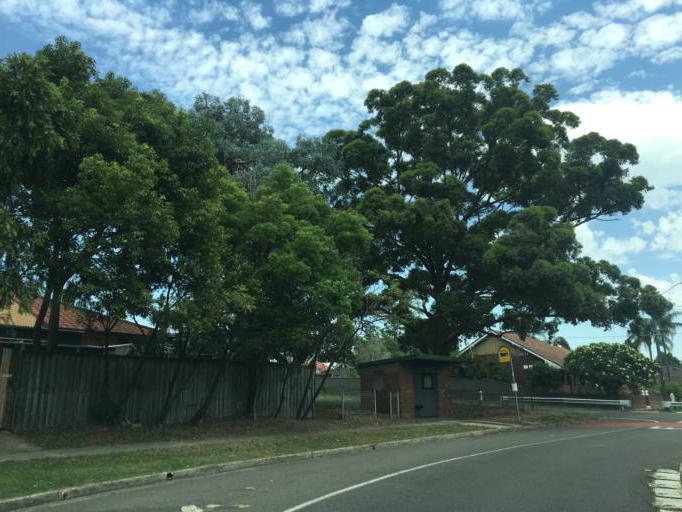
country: AU
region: New South Wales
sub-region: Canada Bay
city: Concord
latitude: -33.8257
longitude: 151.1116
